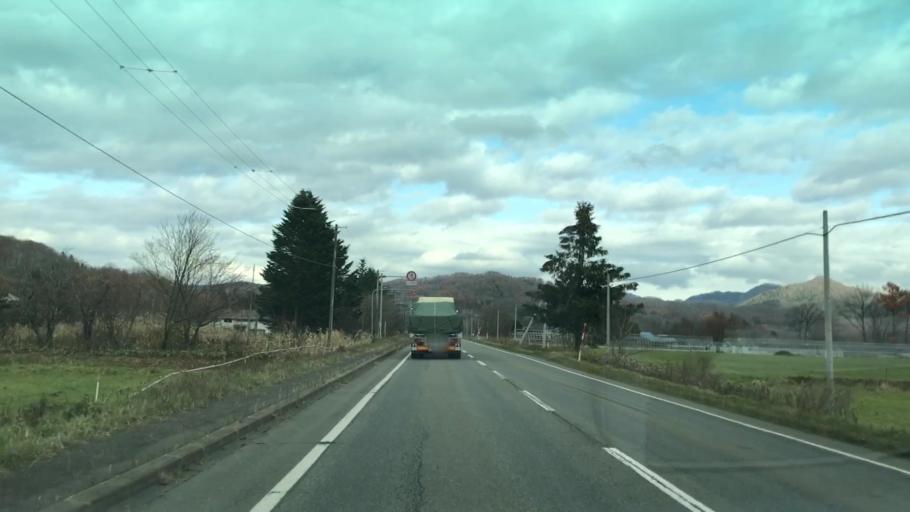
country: JP
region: Hokkaido
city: Shimo-furano
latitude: 42.8714
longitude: 142.4278
